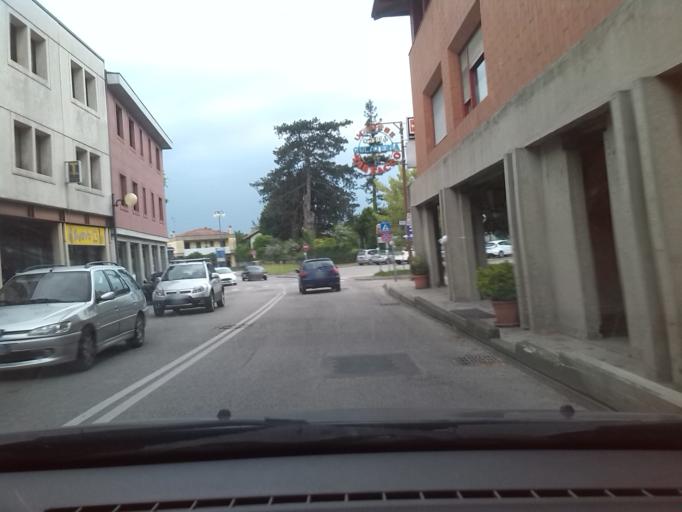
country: IT
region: Friuli Venezia Giulia
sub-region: Provincia di Udine
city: Santo Stefano
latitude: 46.2072
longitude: 13.1252
